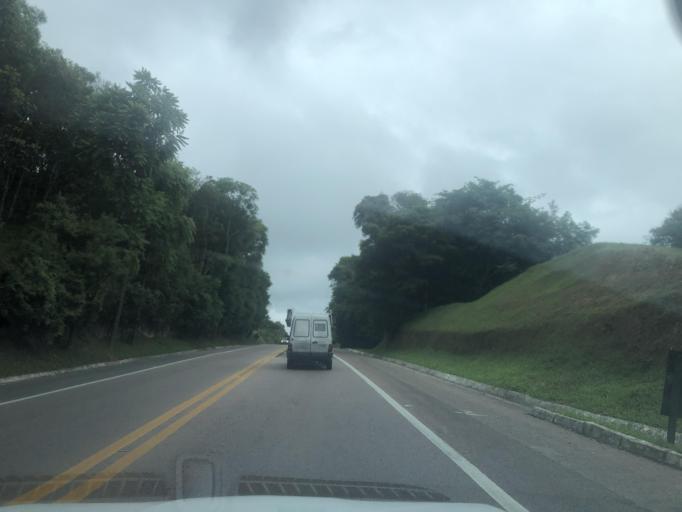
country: BR
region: Parana
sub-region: Araucaria
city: Araucaria
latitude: -25.8519
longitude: -49.3578
